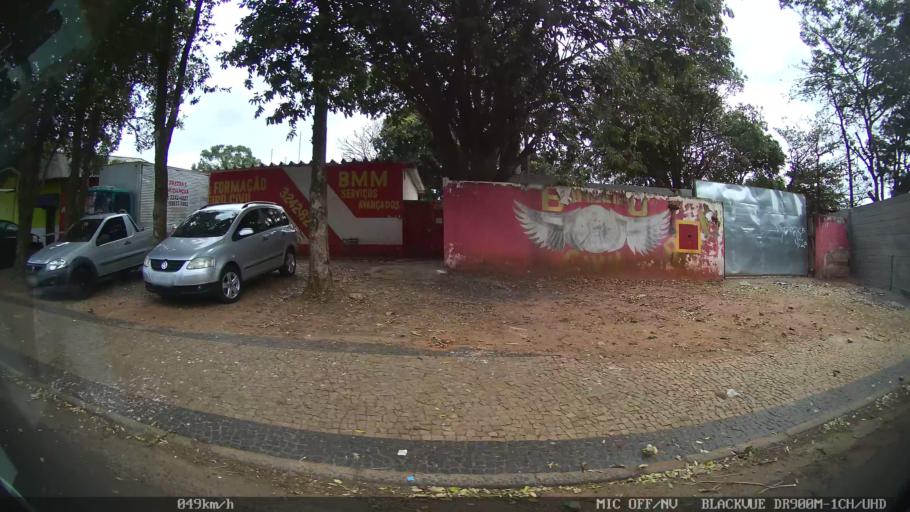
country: BR
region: Sao Paulo
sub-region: Bady Bassitt
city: Bady Bassitt
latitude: -20.8135
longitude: -49.4960
